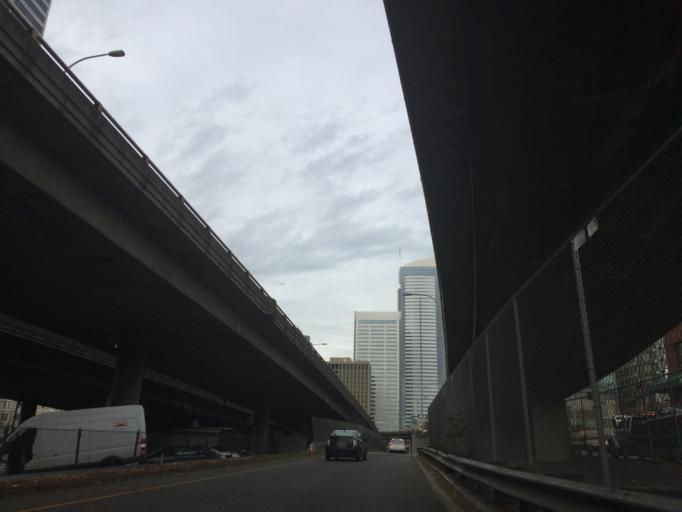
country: US
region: Washington
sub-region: King County
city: Seattle
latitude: 47.6055
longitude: -122.3279
